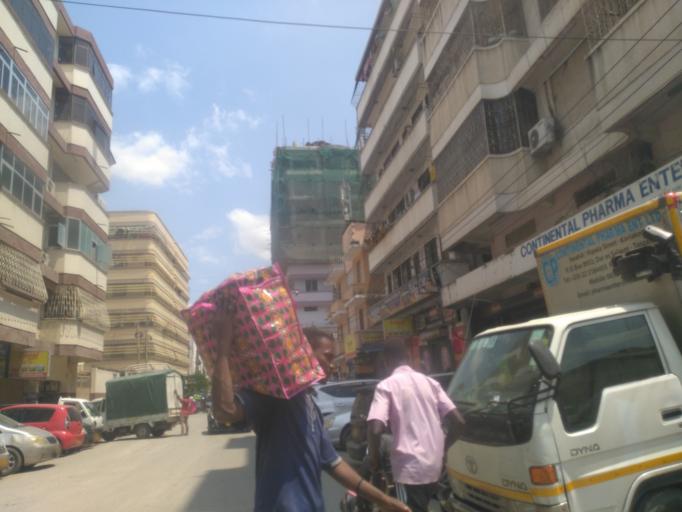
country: TZ
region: Dar es Salaam
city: Dar es Salaam
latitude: -6.8230
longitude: 39.2766
